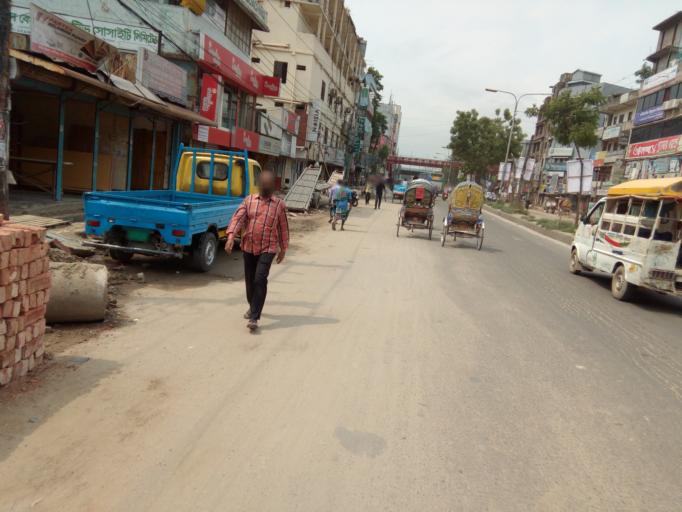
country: BD
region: Dhaka
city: Paltan
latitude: 23.7642
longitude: 90.4209
